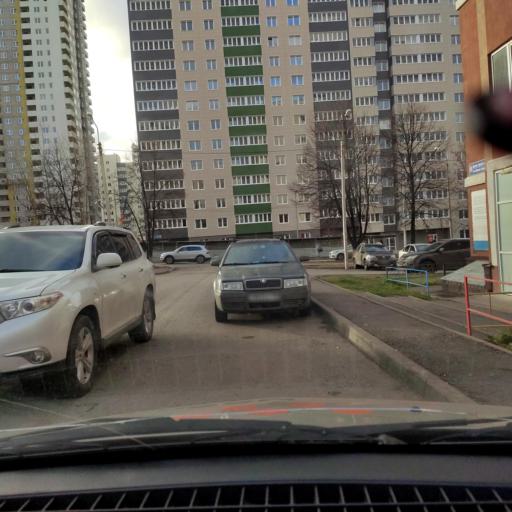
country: RU
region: Bashkortostan
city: Ufa
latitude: 54.8248
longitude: 56.0716
